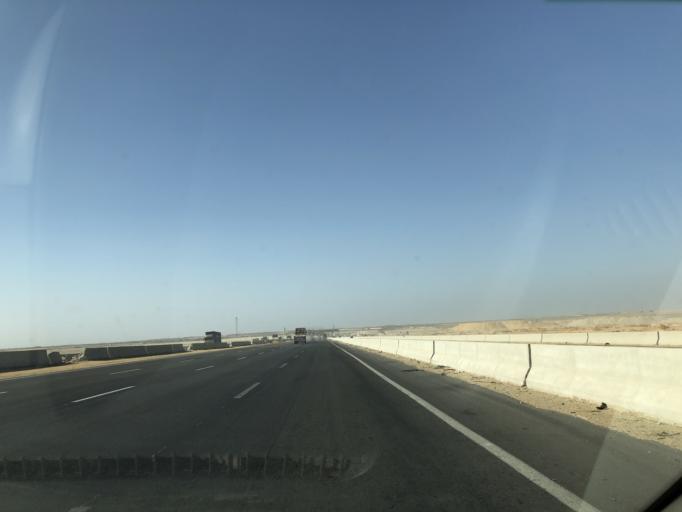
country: EG
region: Muhafazat al Minufiyah
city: Ashmun
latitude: 30.0546
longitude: 30.8460
